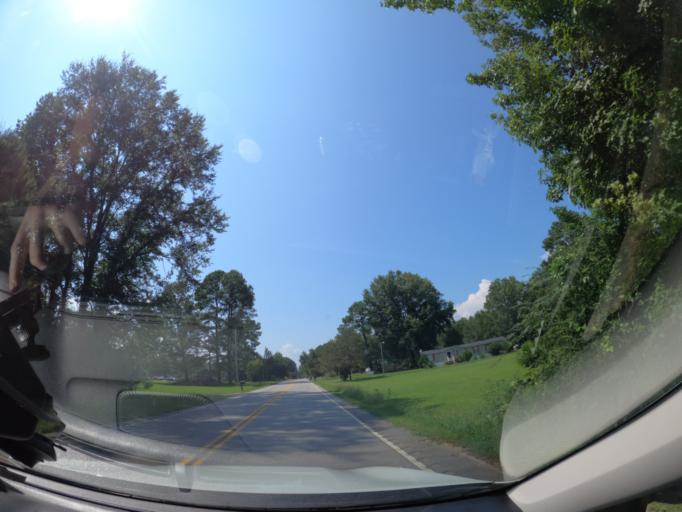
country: US
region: South Carolina
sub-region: Richland County
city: Hopkins
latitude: 33.8453
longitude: -80.8662
